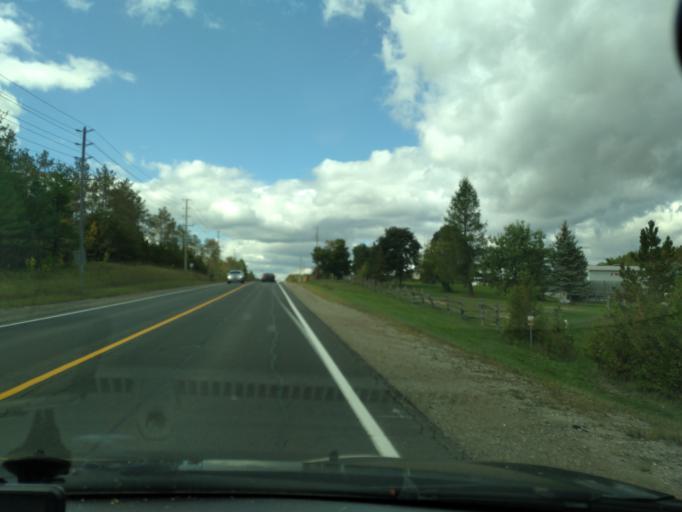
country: CA
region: Ontario
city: Angus
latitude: 44.2542
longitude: -79.7971
